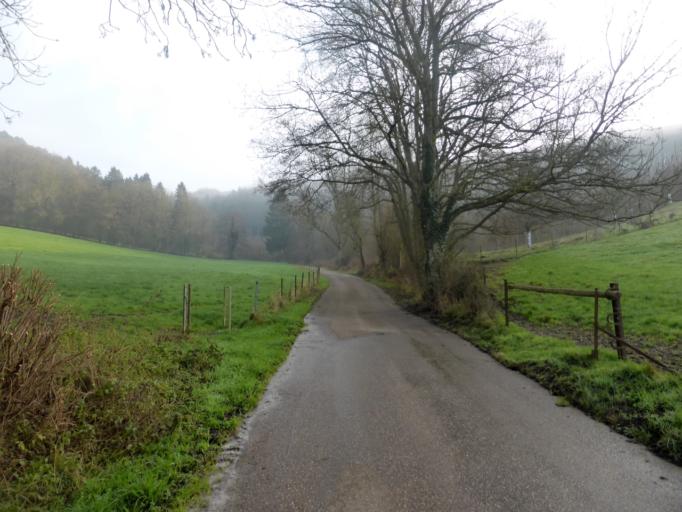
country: LU
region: Luxembourg
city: Rollingen
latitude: 49.7588
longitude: 6.1284
